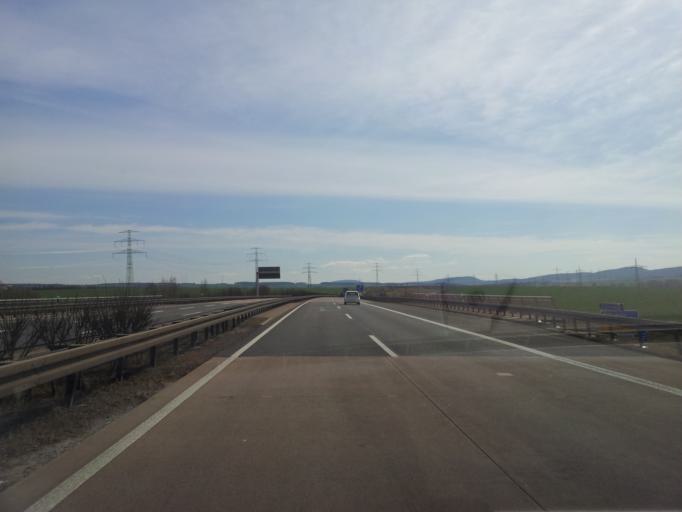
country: DE
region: Thuringia
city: Alkersleben
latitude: 50.8524
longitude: 11.0089
